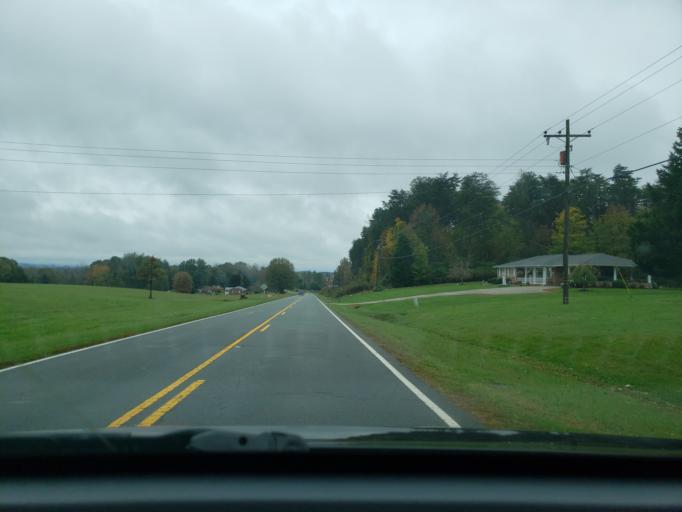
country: US
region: North Carolina
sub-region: Stokes County
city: Walnut Cove
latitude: 36.3409
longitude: -80.1523
